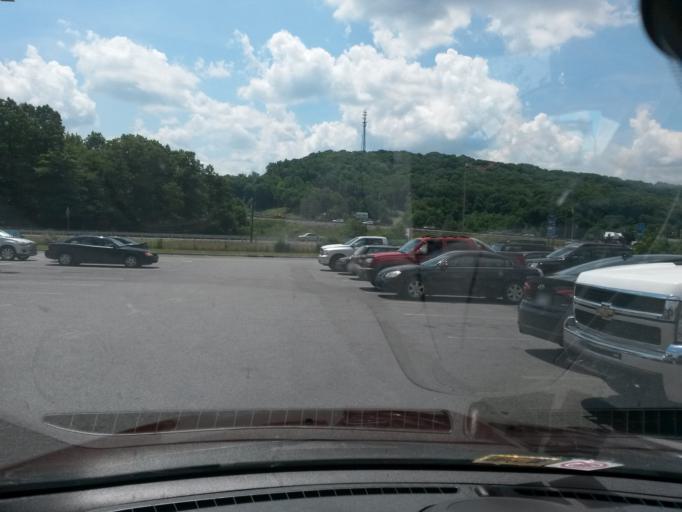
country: US
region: West Virginia
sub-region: Mercer County
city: Princeton
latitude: 37.3649
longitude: -81.0501
